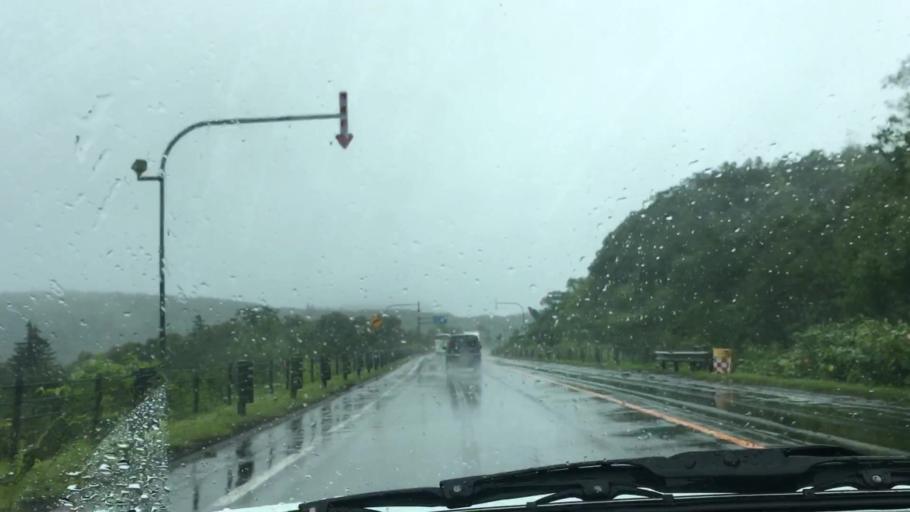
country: JP
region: Hokkaido
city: Sapporo
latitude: 42.8615
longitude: 141.1035
